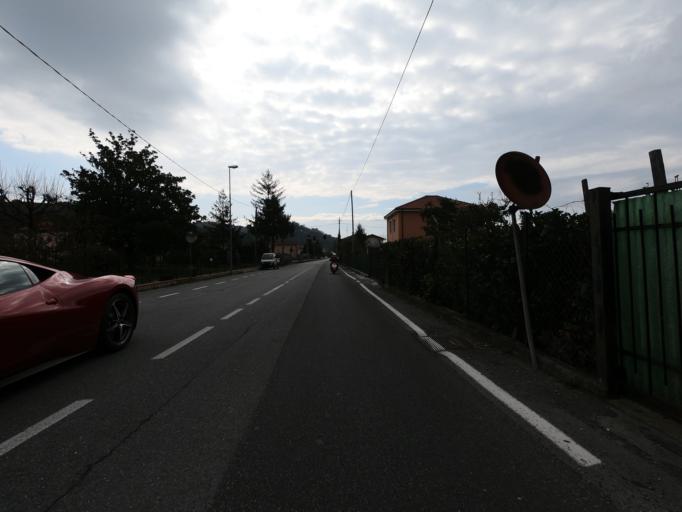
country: IT
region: Liguria
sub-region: Provincia di Savona
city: Andora
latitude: 43.9726
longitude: 8.1380
